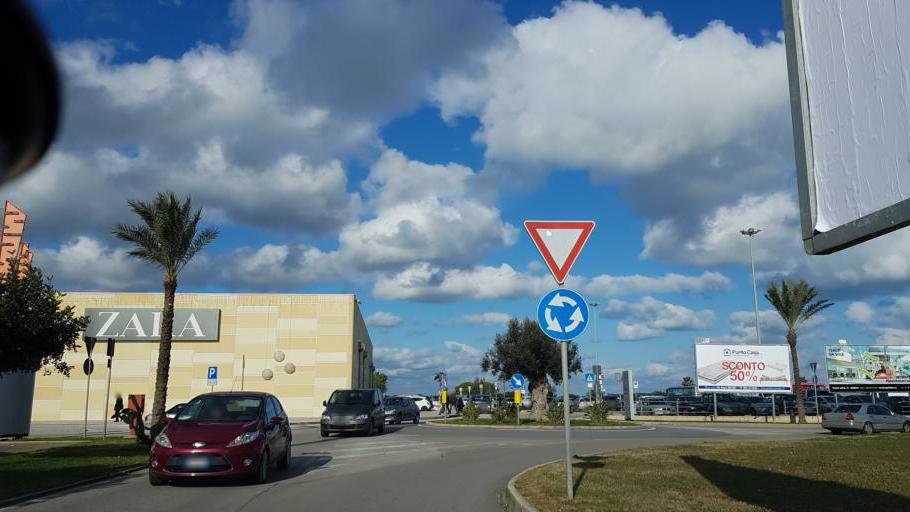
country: IT
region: Apulia
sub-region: Provincia di Brindisi
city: Brindisi
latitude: 40.6185
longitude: 17.9039
